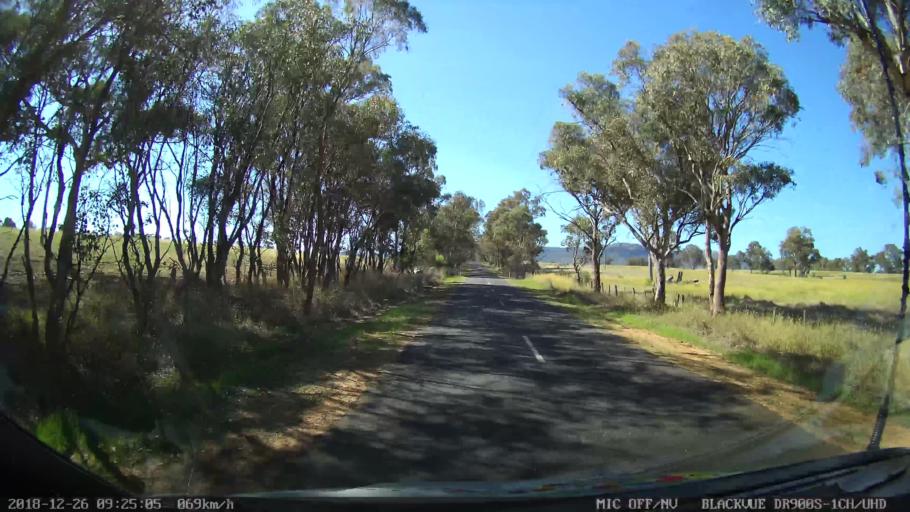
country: AU
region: New South Wales
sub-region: Mid-Western Regional
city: Kandos
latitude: -32.8167
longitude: 150.0022
